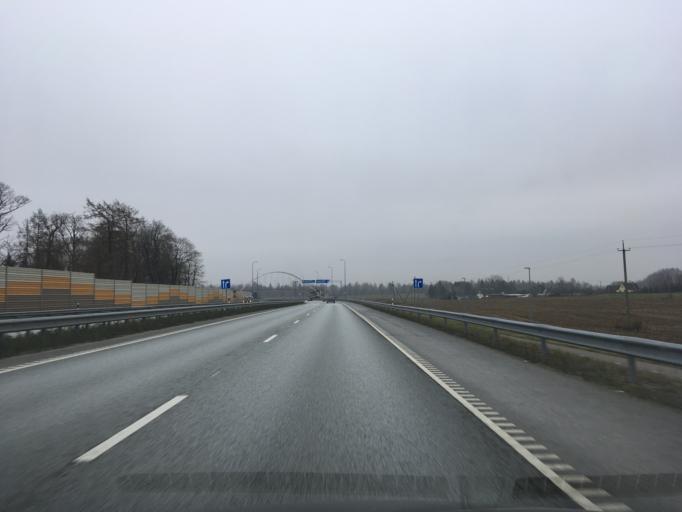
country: EE
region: Ida-Virumaa
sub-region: Johvi vald
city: Johvi
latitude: 59.3724
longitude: 27.3826
